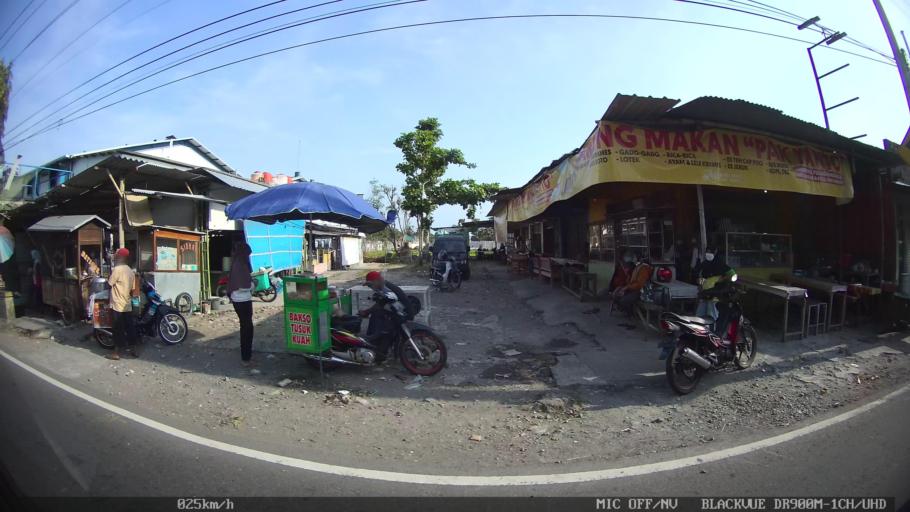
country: ID
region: Daerah Istimewa Yogyakarta
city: Bantul
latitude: -7.8765
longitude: 110.3207
